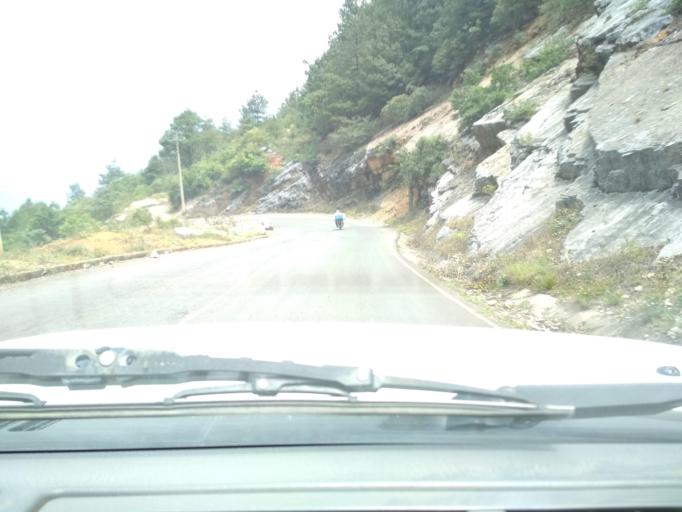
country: MX
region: Veracruz
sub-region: Camerino Z. Mendoza
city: Necoxtla
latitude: 18.7854
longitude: -97.1542
